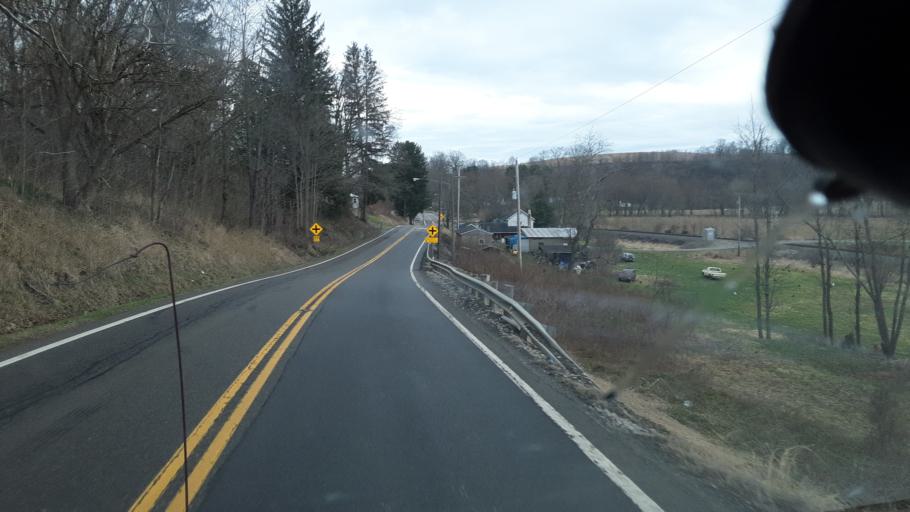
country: US
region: Ohio
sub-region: Coshocton County
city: West Lafayette
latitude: 40.3342
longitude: -81.7405
